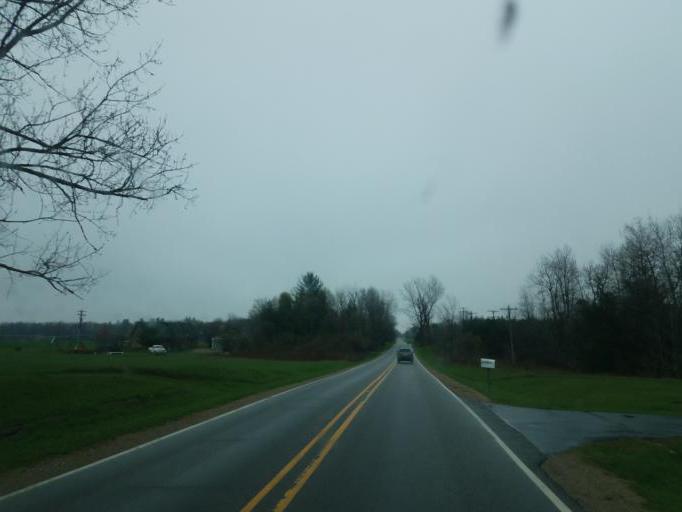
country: US
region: Michigan
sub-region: Isabella County
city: Lake Isabella
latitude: 43.5240
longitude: -84.9990
